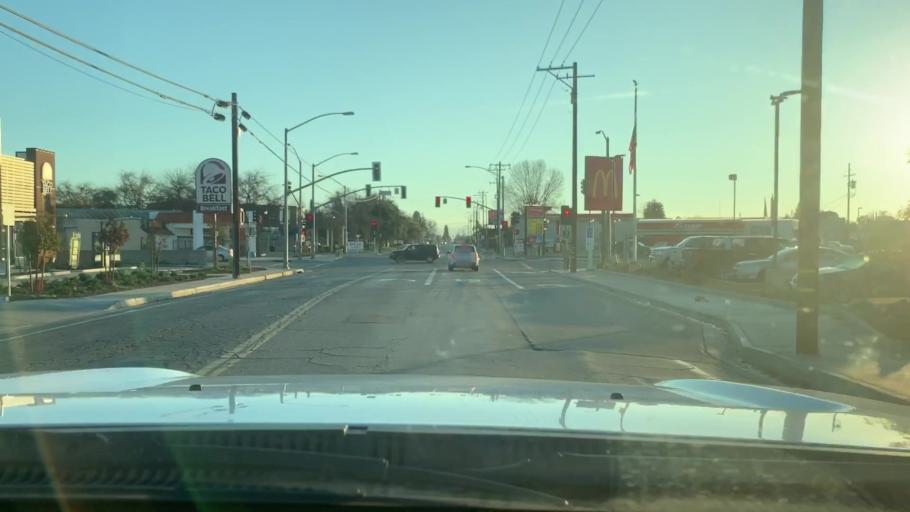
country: US
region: California
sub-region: Kern County
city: Shafter
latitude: 35.4998
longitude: -119.2790
